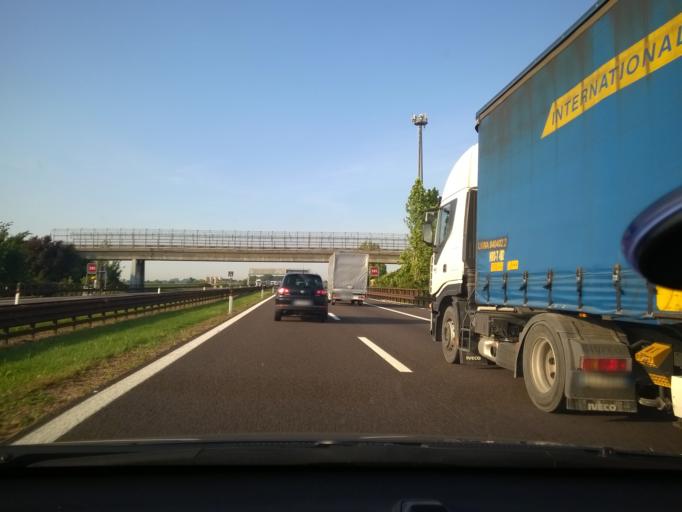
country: IT
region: Lombardy
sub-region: Provincia di Mantova
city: Castelbelforte
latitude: 45.2412
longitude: 10.8642
